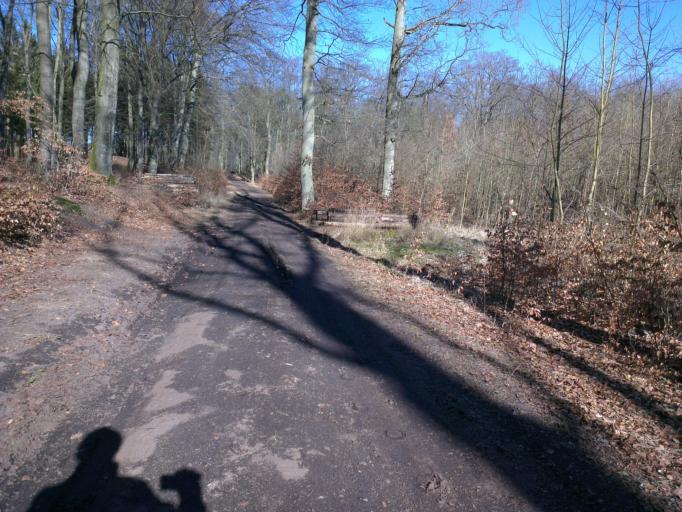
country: DK
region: Capital Region
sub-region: Frederikssund Kommune
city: Jaegerspris
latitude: 55.8777
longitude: 11.9951
